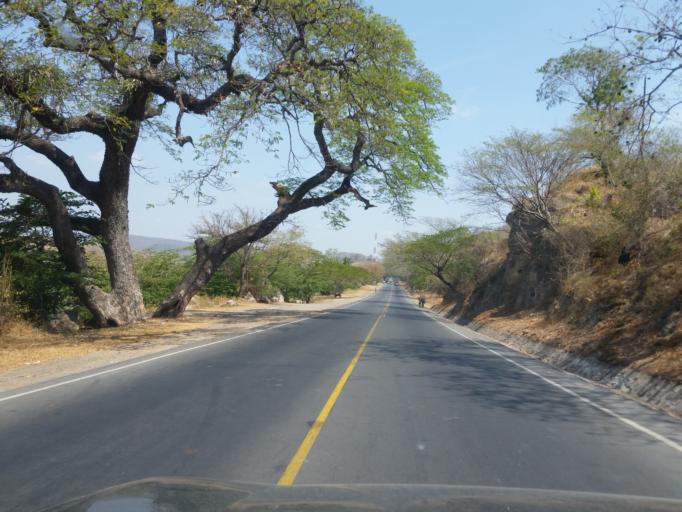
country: NI
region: Matagalpa
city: Terrabona
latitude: 12.5765
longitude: -86.0419
